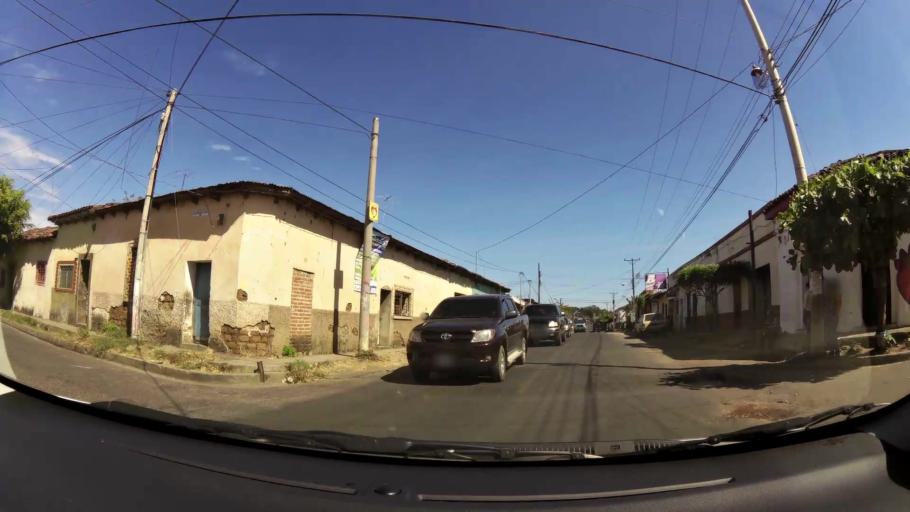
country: SV
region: Santa Ana
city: Chalchuapa
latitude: 13.9817
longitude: -89.6819
